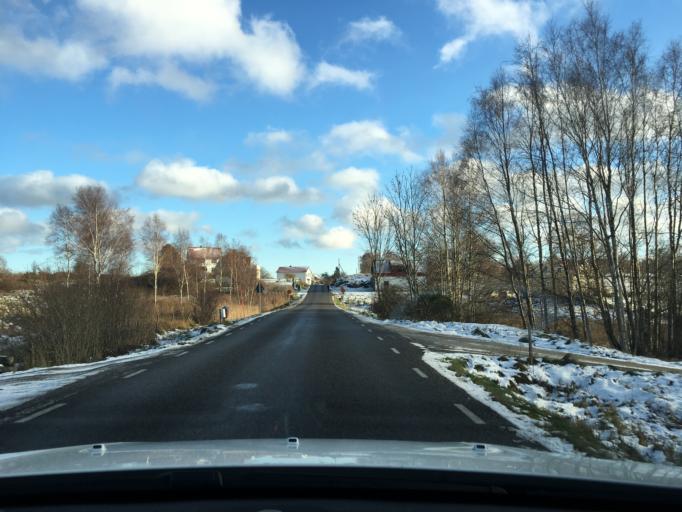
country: SE
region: Vaestra Goetaland
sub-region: Tjorns Kommun
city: Myggenas
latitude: 58.0519
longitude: 11.7069
